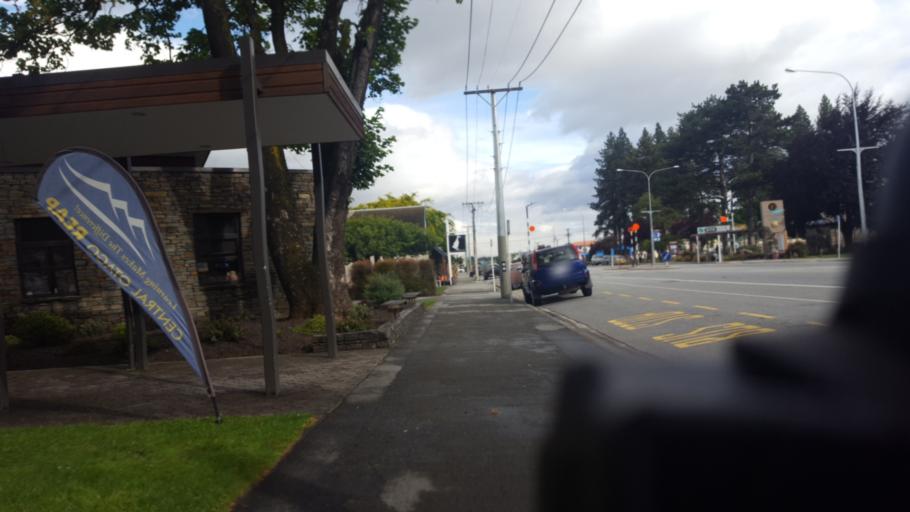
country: NZ
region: Otago
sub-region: Queenstown-Lakes District
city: Wanaka
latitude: -45.2548
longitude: 169.3917
